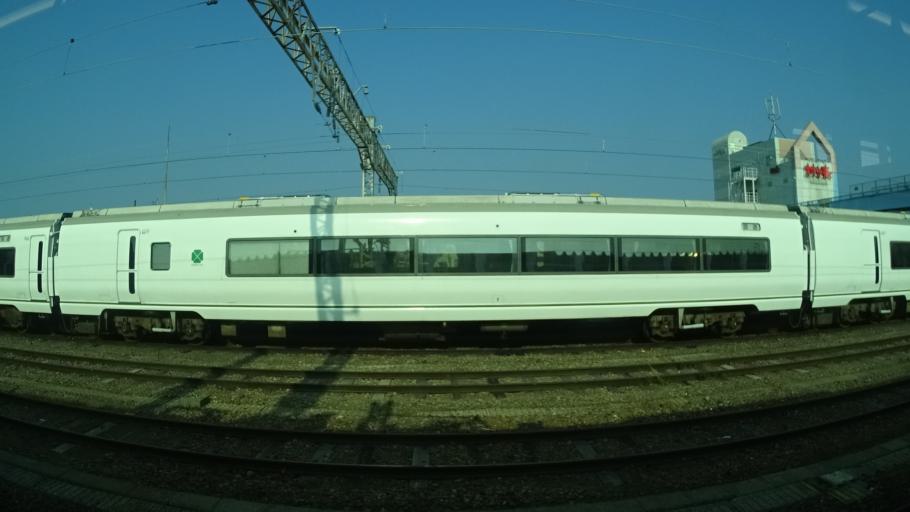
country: JP
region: Ibaraki
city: Takahagi
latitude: 36.7146
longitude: 140.7173
